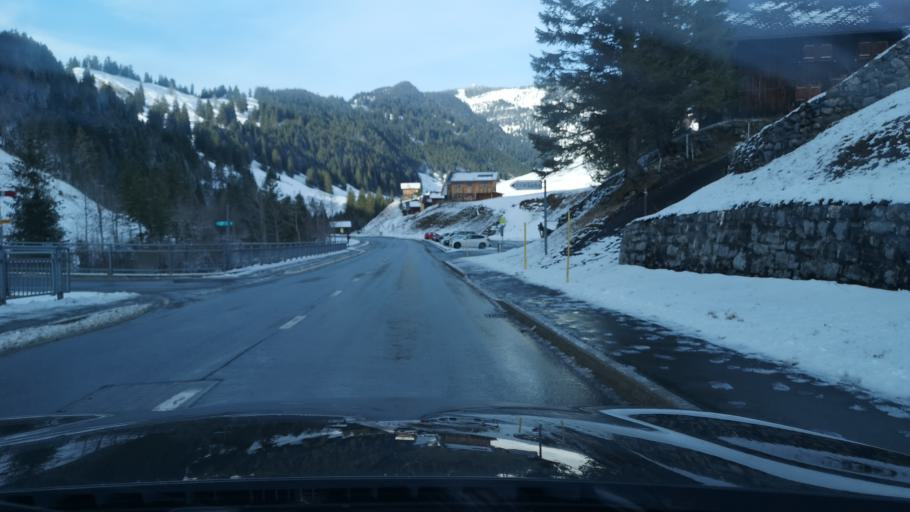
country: LI
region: Triesenberg
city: Triesenberg
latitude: 47.1132
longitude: 9.5721
